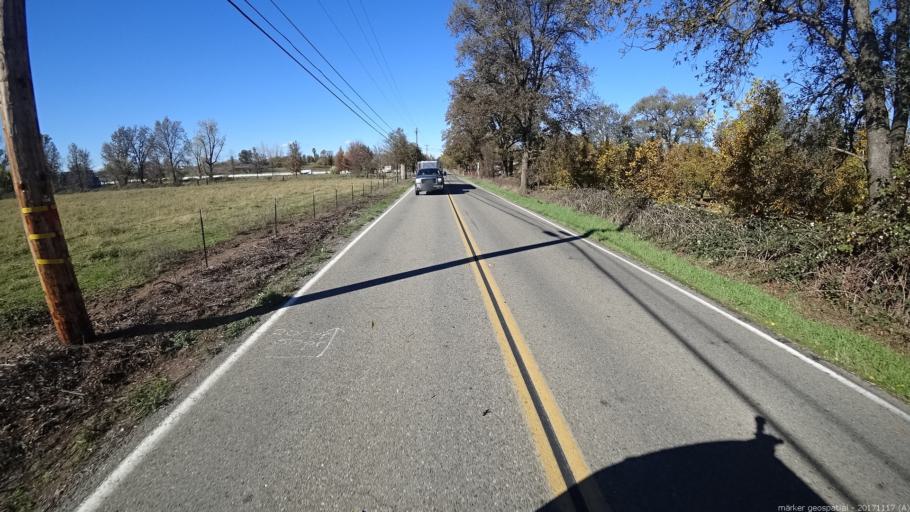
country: US
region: California
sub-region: Shasta County
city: Cottonwood
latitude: 40.4201
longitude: -122.2166
